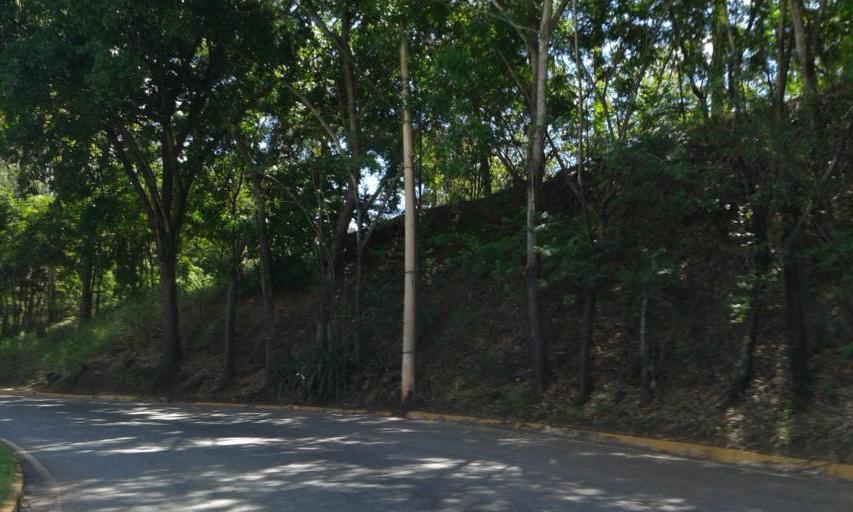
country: BR
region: Minas Gerais
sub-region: Itabira
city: Itabira
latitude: -19.6348
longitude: -43.2382
